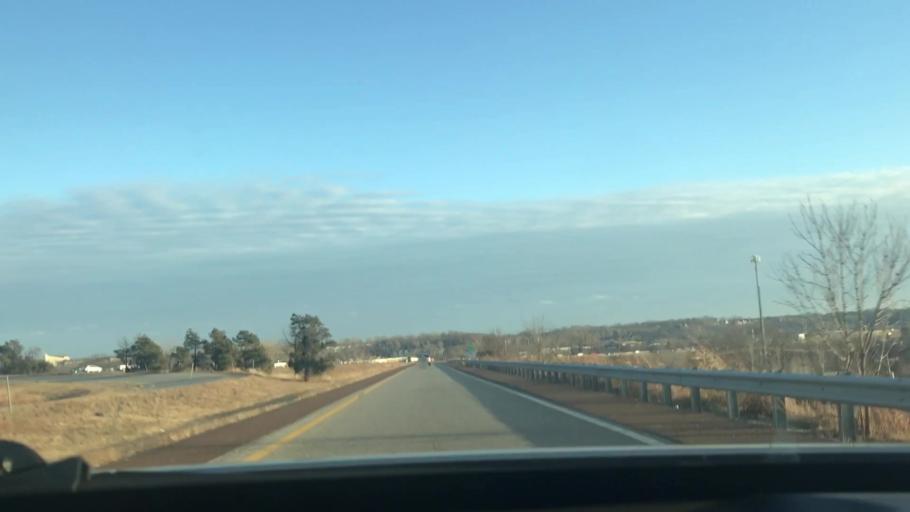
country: US
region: Missouri
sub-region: Jackson County
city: East Independence
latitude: 39.0402
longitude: -94.3650
